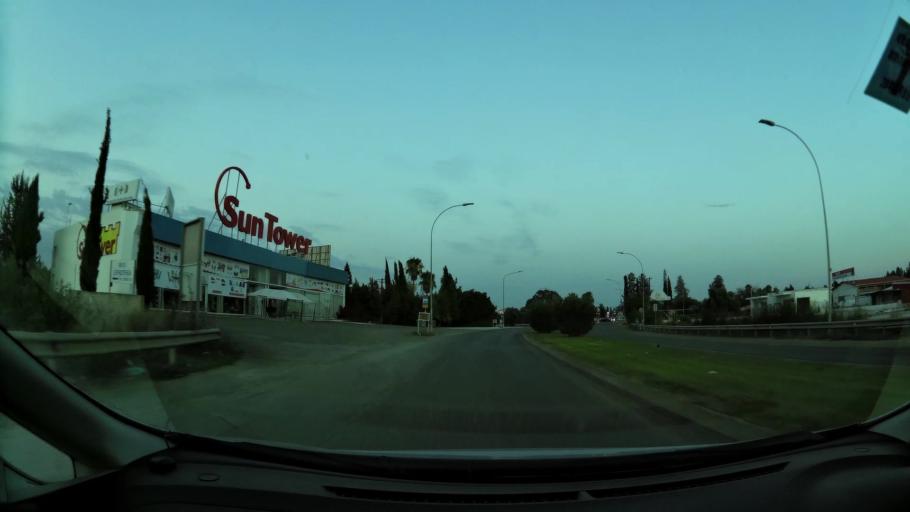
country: CY
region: Lefkosia
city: Nicosia
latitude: 35.1478
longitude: 33.3227
